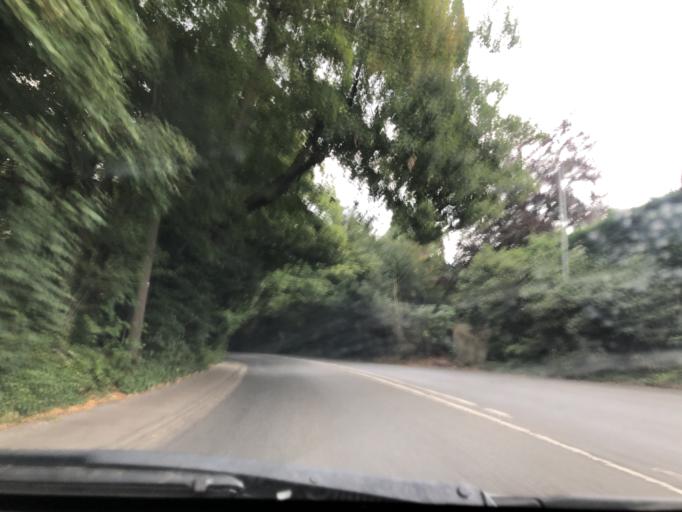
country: GB
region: England
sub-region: Kent
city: Sevenoaks
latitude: 51.2533
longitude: 0.1992
